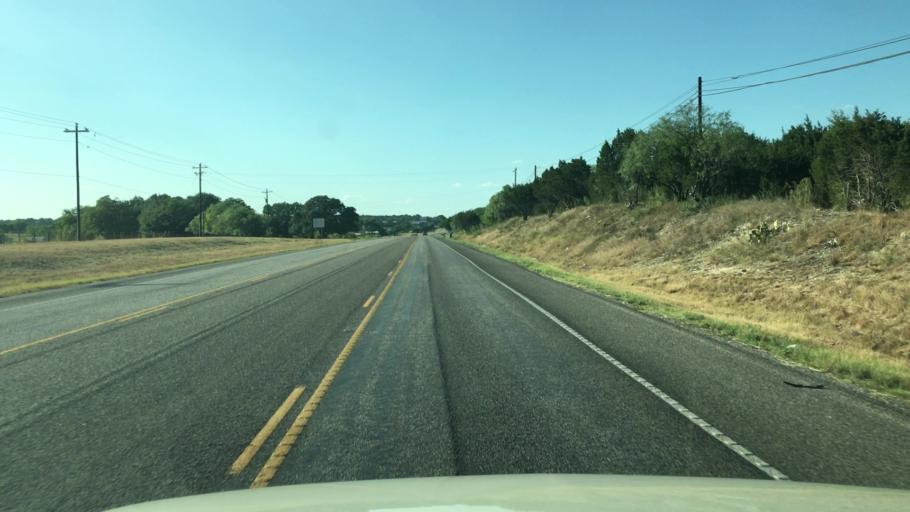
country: US
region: Texas
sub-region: Burnet County
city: Burnet
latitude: 30.7851
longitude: -98.2356
